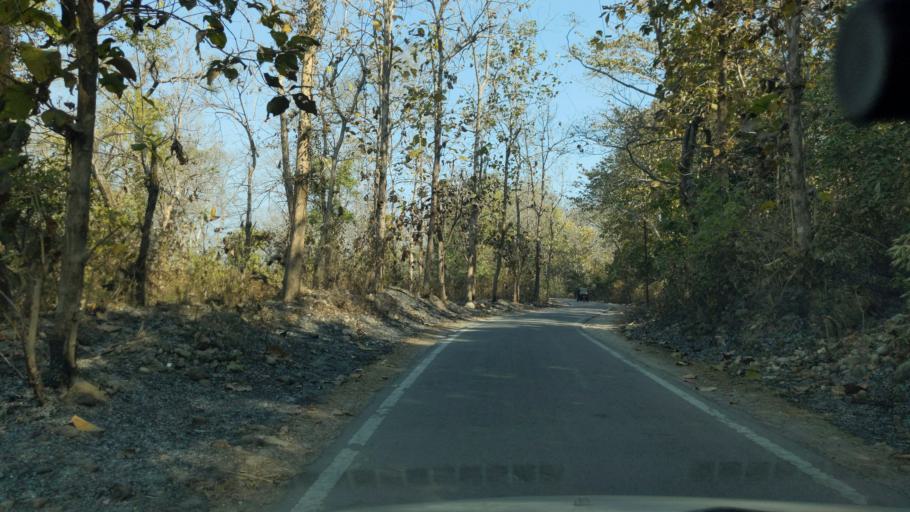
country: IN
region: Uttarakhand
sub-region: Naini Tal
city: Ramnagar
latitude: 29.4008
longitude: 79.1356
